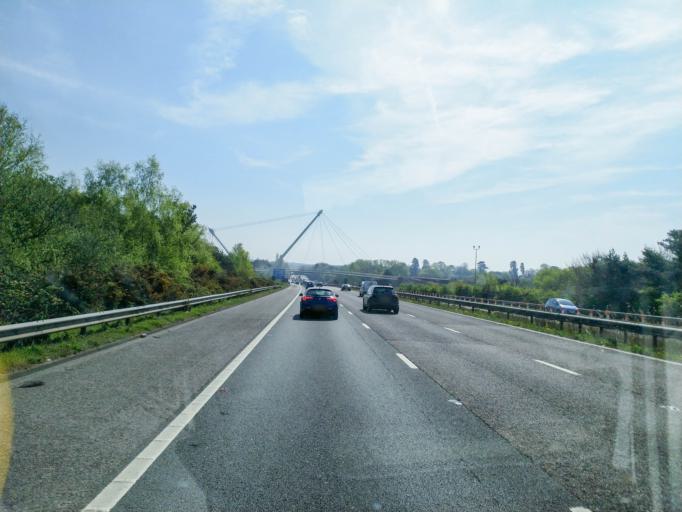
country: GB
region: England
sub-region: Kent
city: Ashford
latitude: 51.1603
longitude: 0.8691
